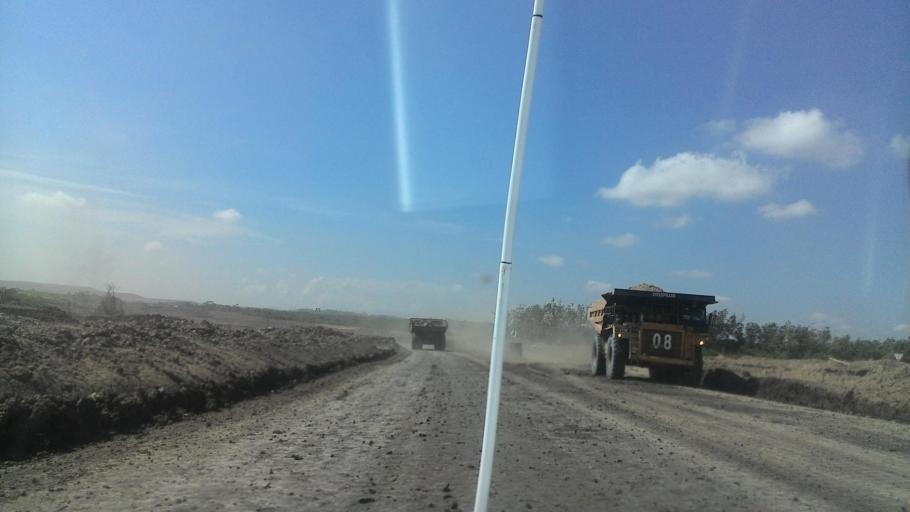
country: ID
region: South Kalimantan
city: Tanta
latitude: -2.1852
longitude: 115.4719
